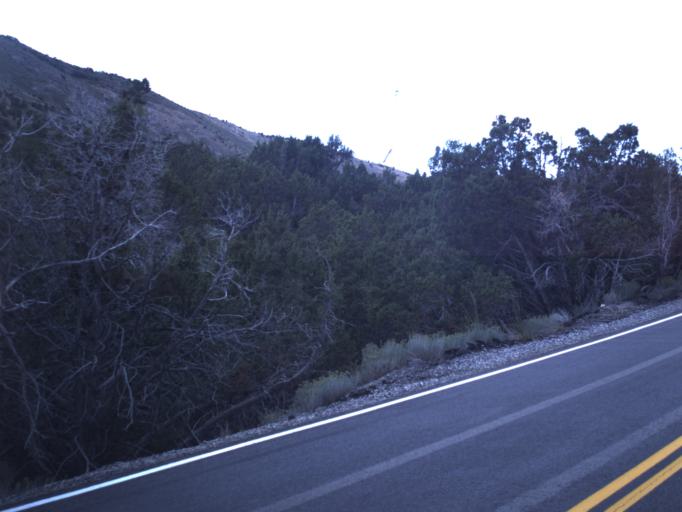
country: US
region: Utah
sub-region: Tooele County
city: Grantsville
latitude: 40.3367
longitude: -112.5717
